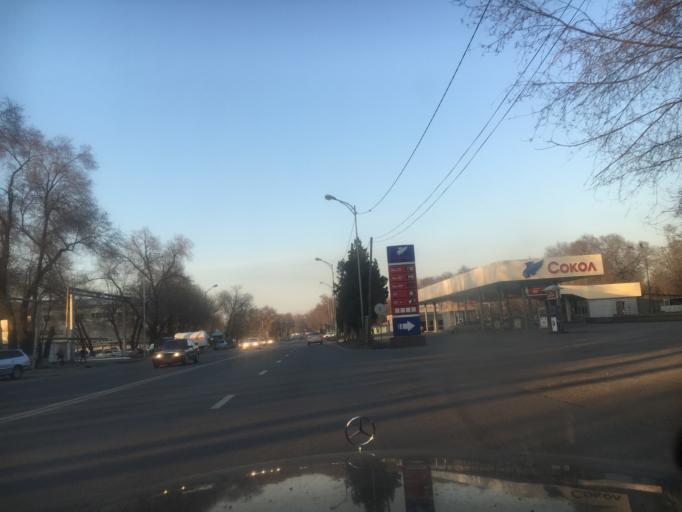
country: KZ
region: Almaty Oblysy
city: Pervomayskiy
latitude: 43.3624
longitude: 76.9826
